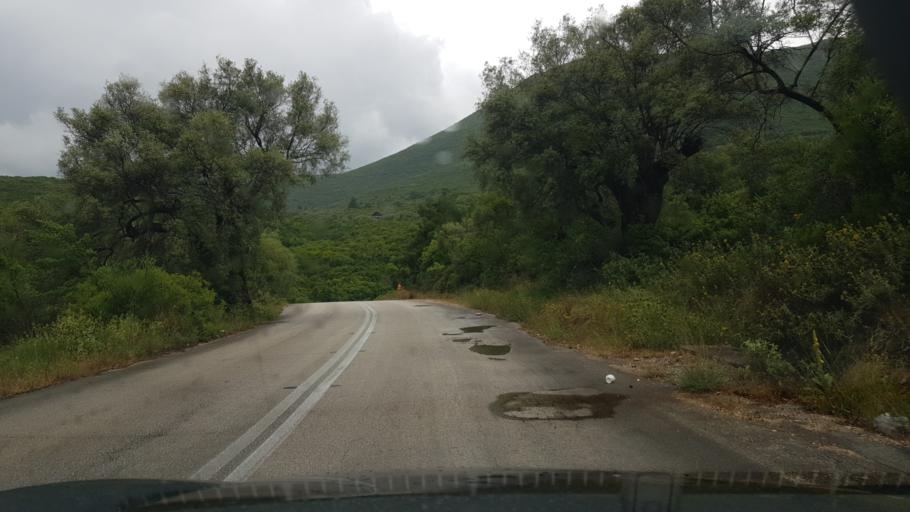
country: GR
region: Ionian Islands
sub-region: Lefkada
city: Nidri
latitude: 38.6489
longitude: 20.6779
